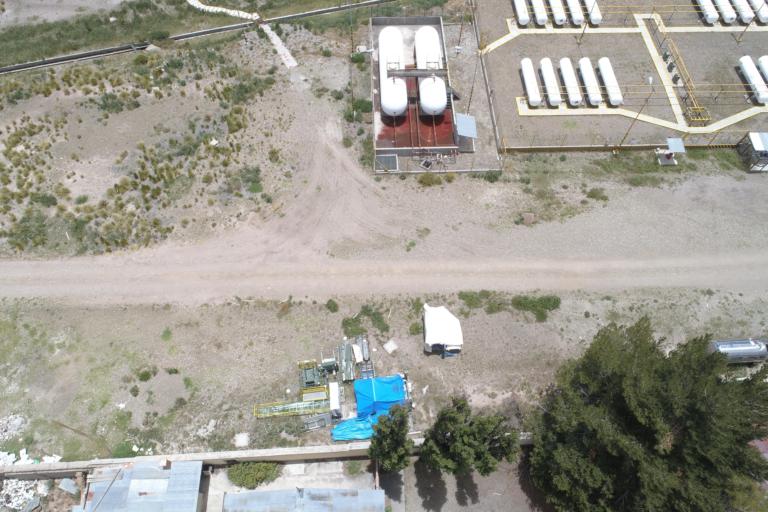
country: BO
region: Oruro
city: Challapata
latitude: -19.0107
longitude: -66.7806
